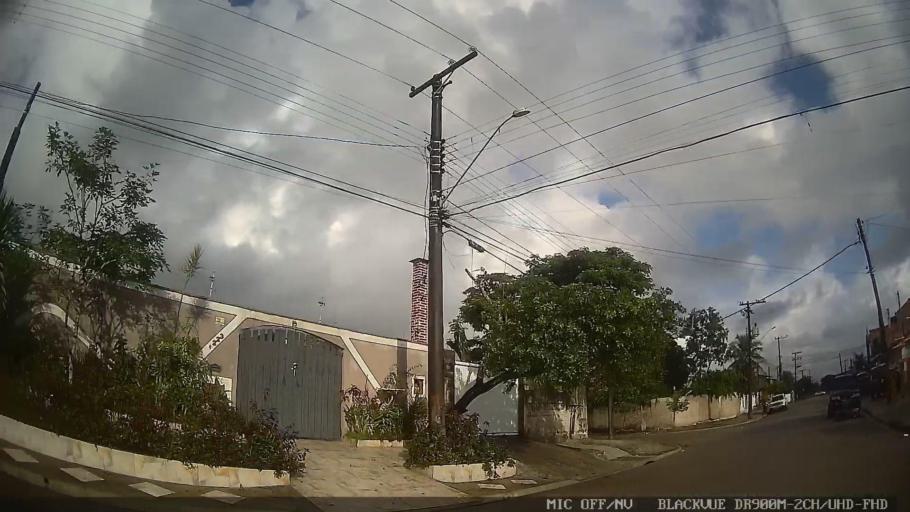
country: BR
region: Sao Paulo
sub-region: Itanhaem
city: Itanhaem
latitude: -24.1859
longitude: -46.8588
